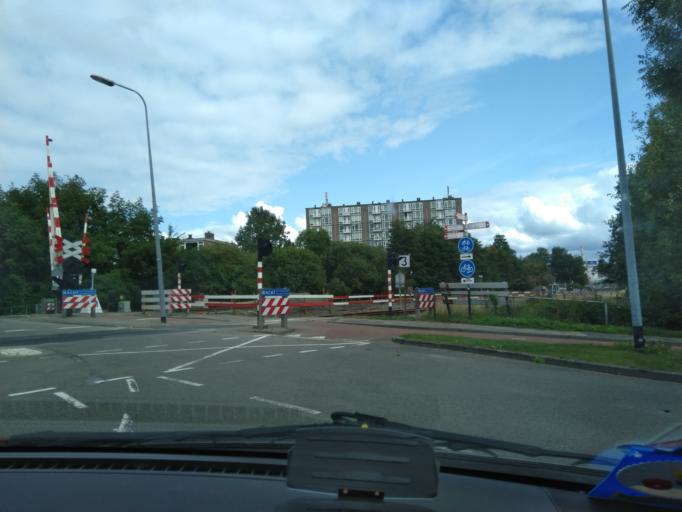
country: NL
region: Groningen
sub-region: Gemeente Groningen
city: Groningen
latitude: 53.2099
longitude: 6.5494
